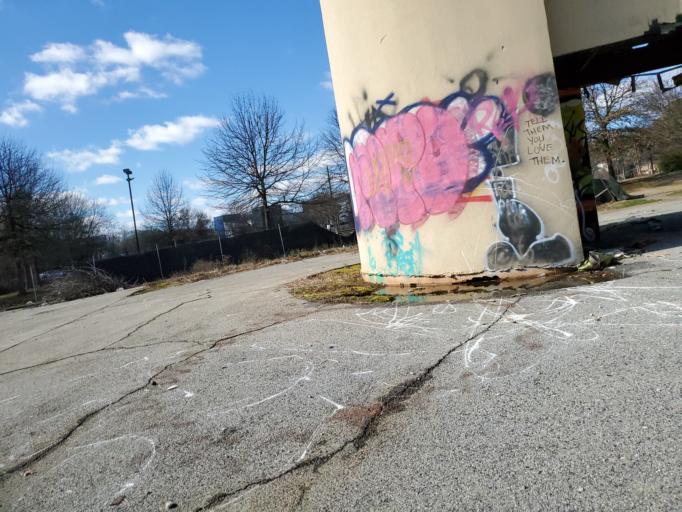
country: US
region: Georgia
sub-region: DeKalb County
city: Druid Hills
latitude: 33.7456
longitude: -84.3325
